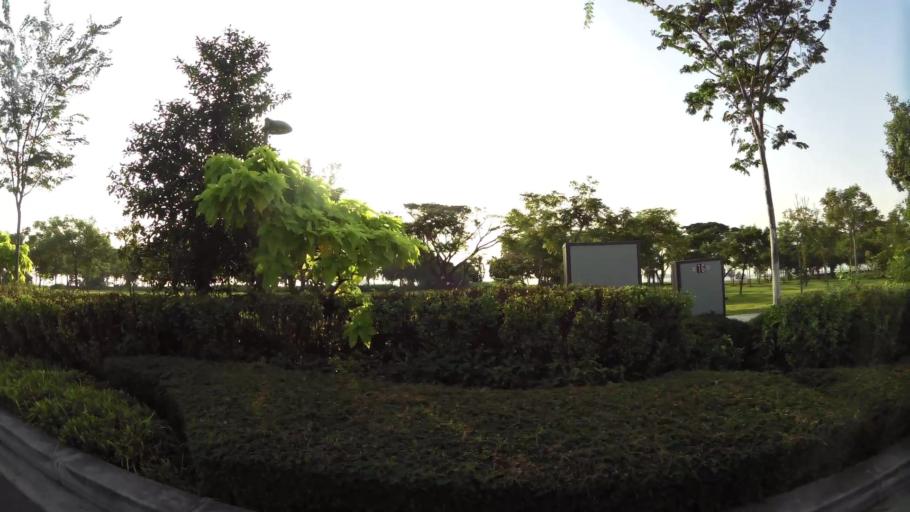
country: SG
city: Singapore
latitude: 1.2772
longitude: 103.8698
